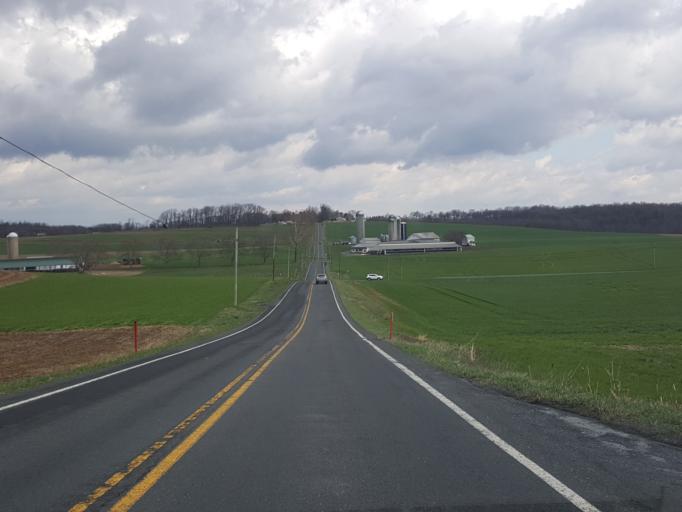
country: US
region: Pennsylvania
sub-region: Berks County
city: Robesonia
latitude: 40.3660
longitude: -76.1392
